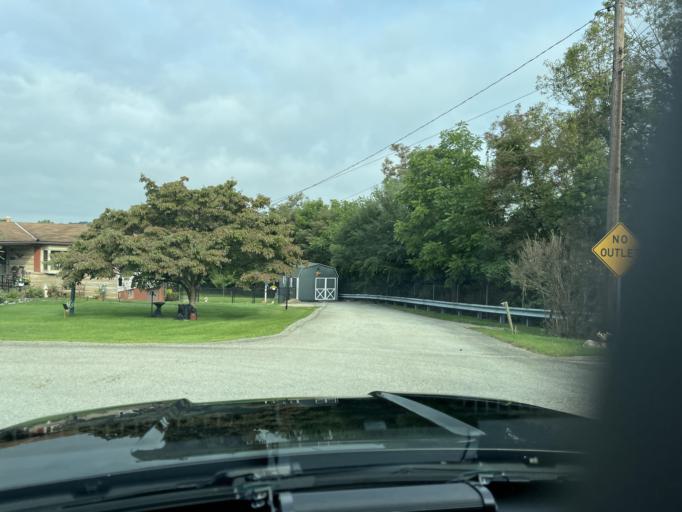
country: US
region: Pennsylvania
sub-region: Fayette County
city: Hopwood
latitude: 39.8715
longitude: -79.7033
